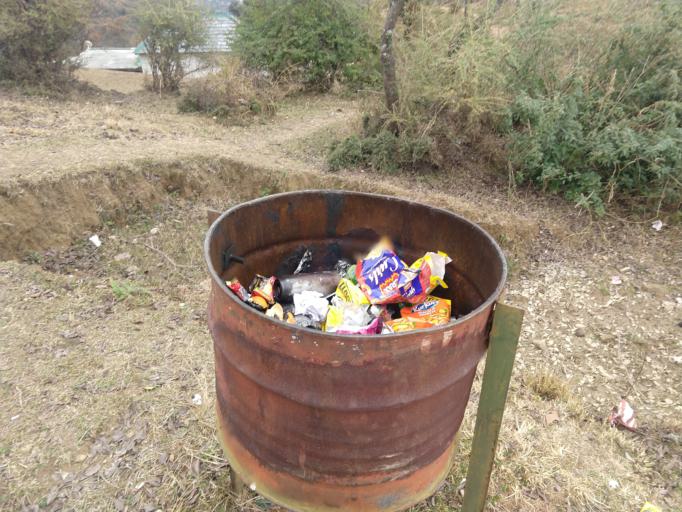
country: IN
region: Himachal Pradesh
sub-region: Kangra
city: Dharmsala
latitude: 32.2201
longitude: 76.3350
